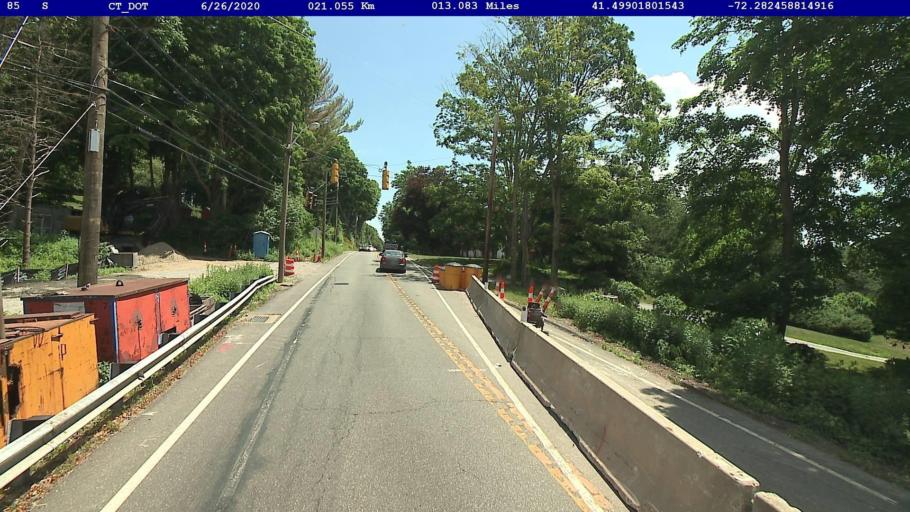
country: US
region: Connecticut
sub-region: New London County
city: Colchester
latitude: 41.4990
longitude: -72.2824
